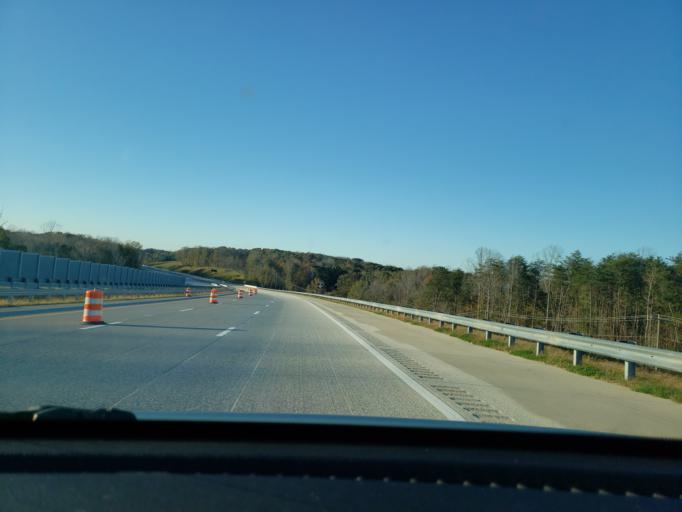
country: US
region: North Carolina
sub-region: Forsyth County
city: Walkertown
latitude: 36.1325
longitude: -80.1322
